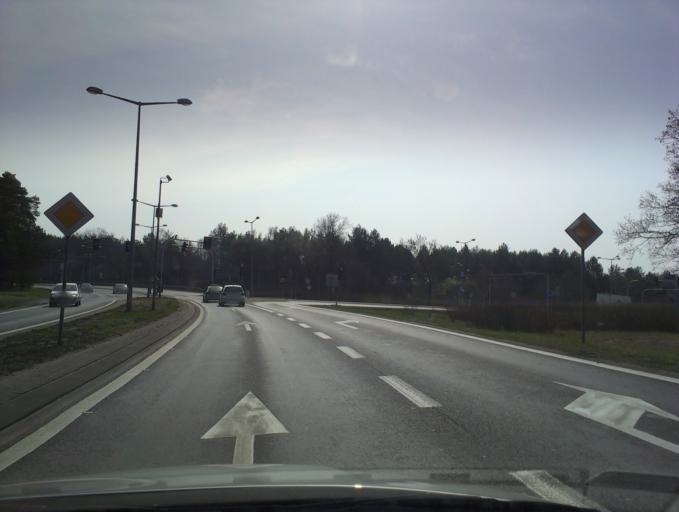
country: PL
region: Greater Poland Voivodeship
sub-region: Powiat pilski
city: Pila
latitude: 53.1507
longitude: 16.7892
